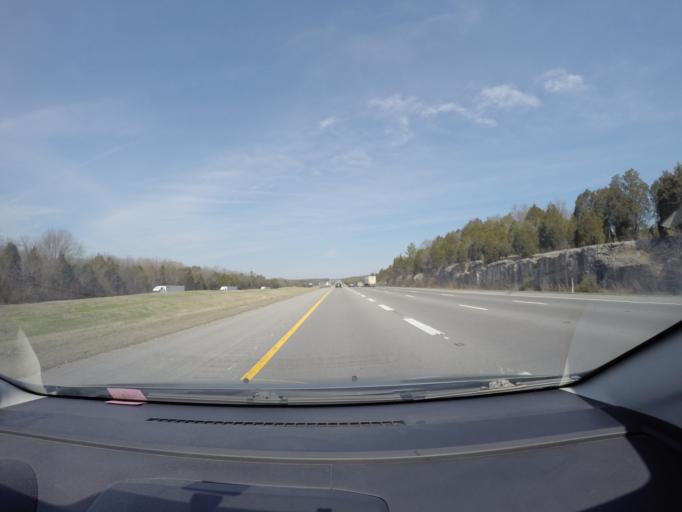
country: US
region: Tennessee
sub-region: Rutherford County
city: Smyrna
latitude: 35.9433
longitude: -86.5412
